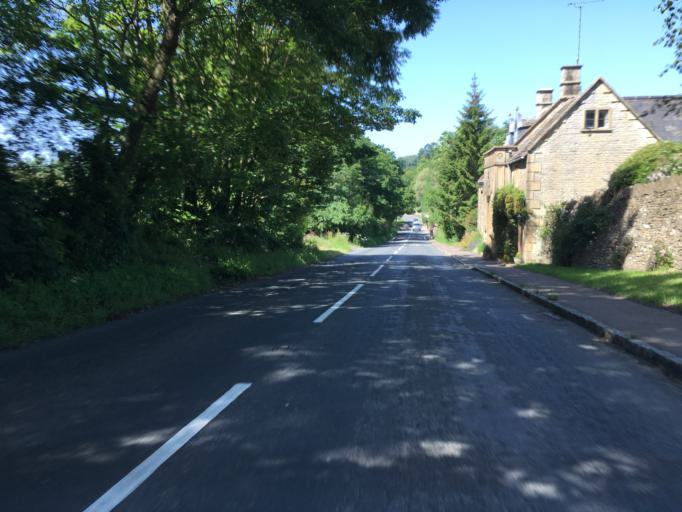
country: GB
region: England
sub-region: Gloucestershire
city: Stow on the Wold
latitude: 51.9298
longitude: -1.7401
